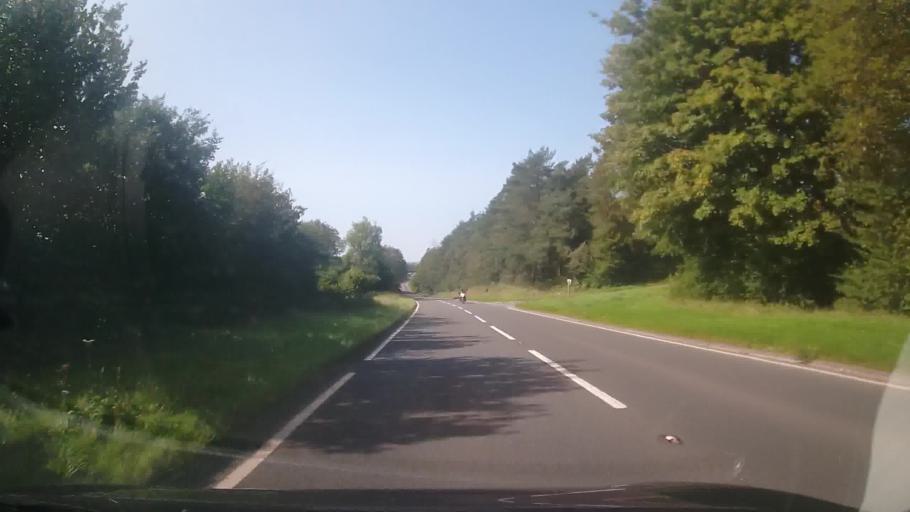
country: GB
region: Wales
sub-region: Sir Powys
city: Builth Wells
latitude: 52.1410
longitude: -3.5027
